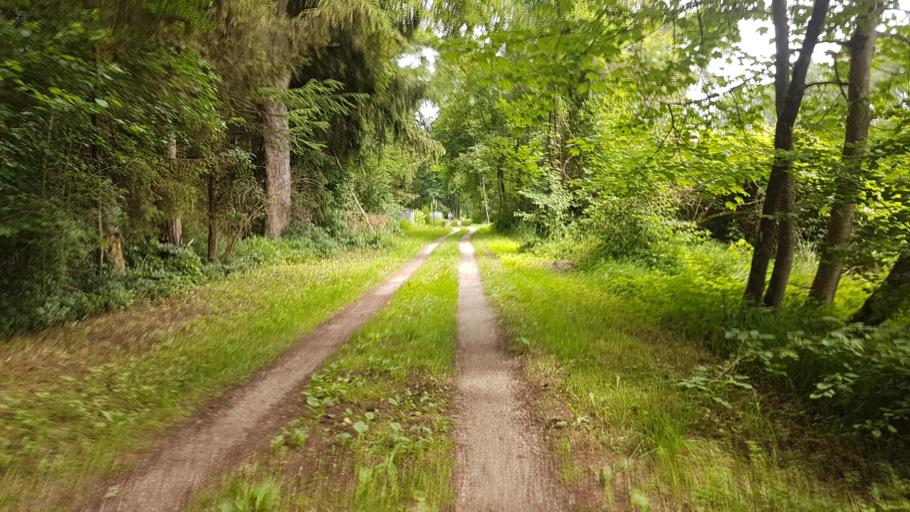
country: DE
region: Bavaria
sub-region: Swabia
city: Gundremmingen
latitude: 48.5150
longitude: 10.3870
